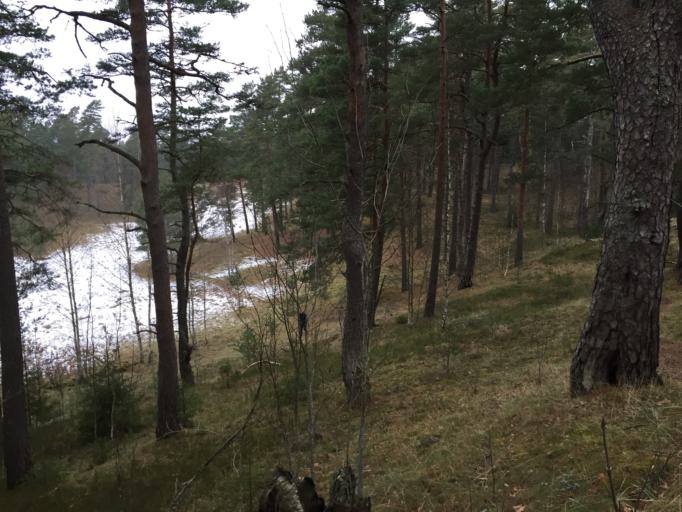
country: EE
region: Saare
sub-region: Kuressaare linn
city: Kuressaare
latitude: 58.3991
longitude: 22.2530
